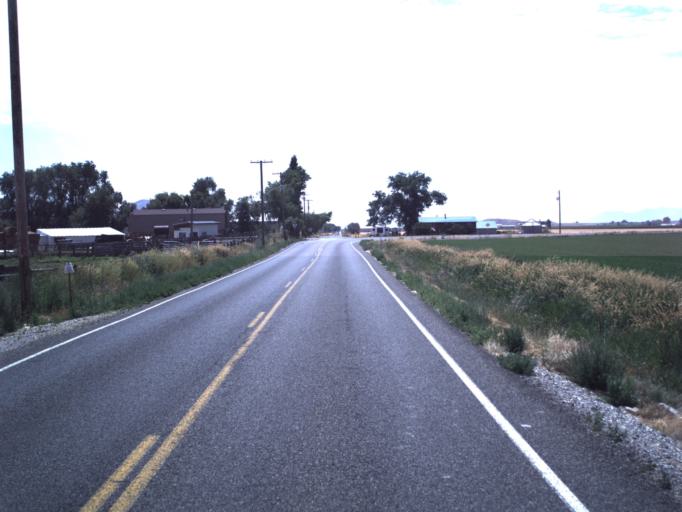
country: US
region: Utah
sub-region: Box Elder County
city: Tremonton
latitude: 41.6965
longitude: -112.2778
